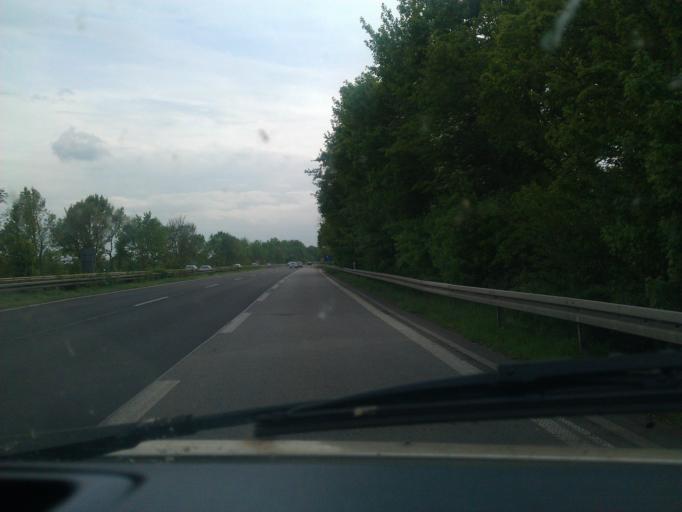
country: DE
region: North Rhine-Westphalia
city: Julich
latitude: 50.9286
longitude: 6.3376
